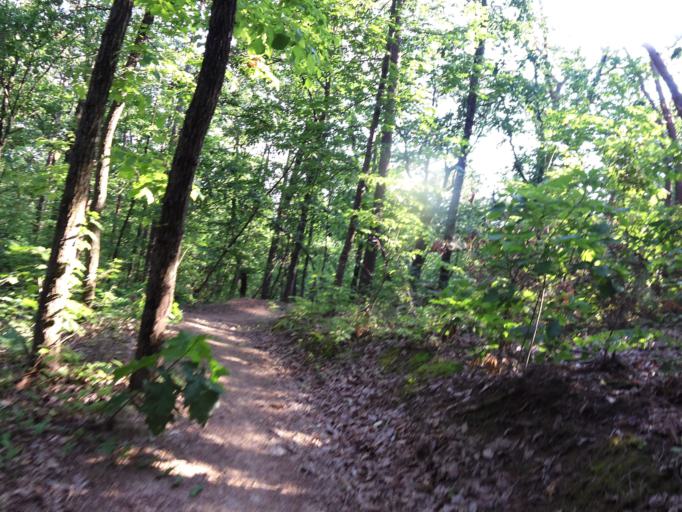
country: US
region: Tennessee
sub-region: Knox County
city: Knoxville
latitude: 36.0069
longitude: -83.9354
